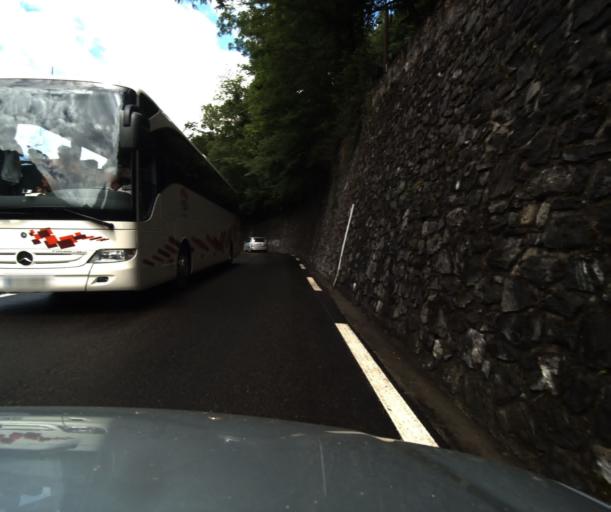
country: FR
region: Midi-Pyrenees
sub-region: Departement des Hautes-Pyrenees
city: Luz-Saint-Sauveur
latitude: 42.8586
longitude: -0.0049
